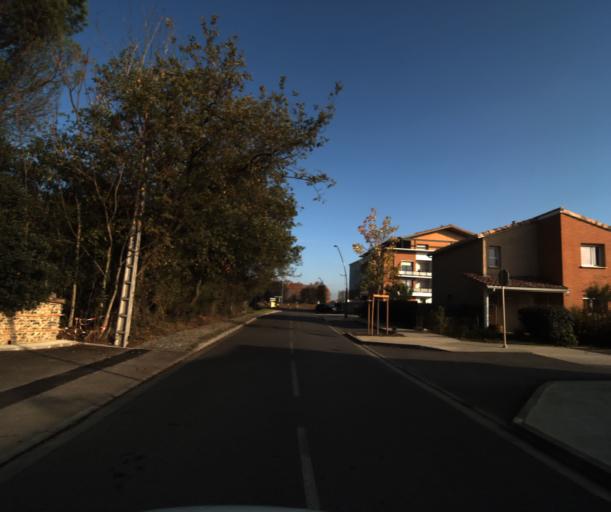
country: FR
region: Midi-Pyrenees
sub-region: Departement de la Haute-Garonne
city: Colomiers
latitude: 43.5948
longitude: 1.3466
